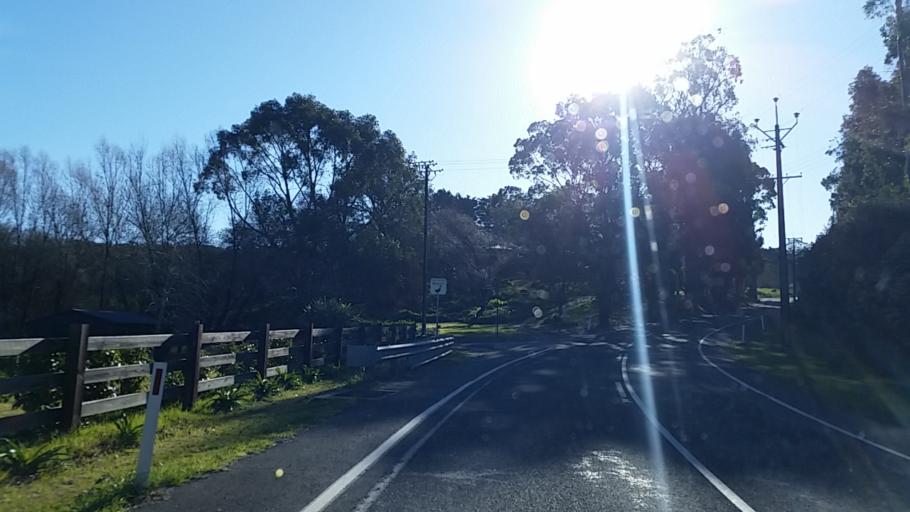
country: AU
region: South Australia
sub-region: Adelaide Hills
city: Crafers
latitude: -34.9586
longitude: 138.7211
